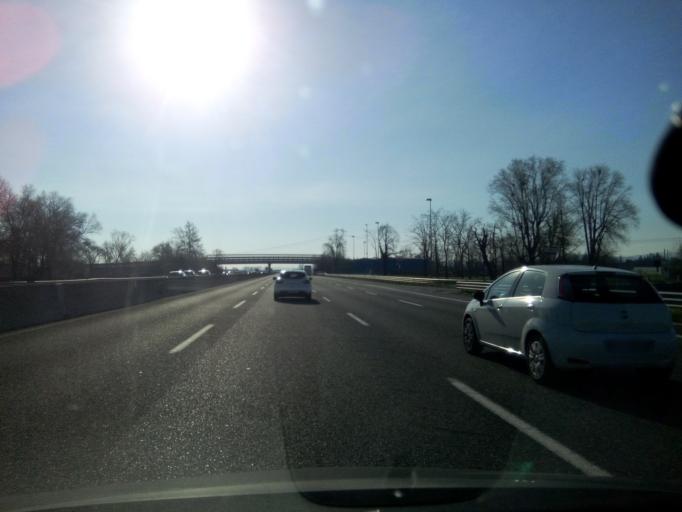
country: IT
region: Emilia-Romagna
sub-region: Provincia di Modena
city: Piumazzo
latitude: 44.5589
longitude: 11.0592
